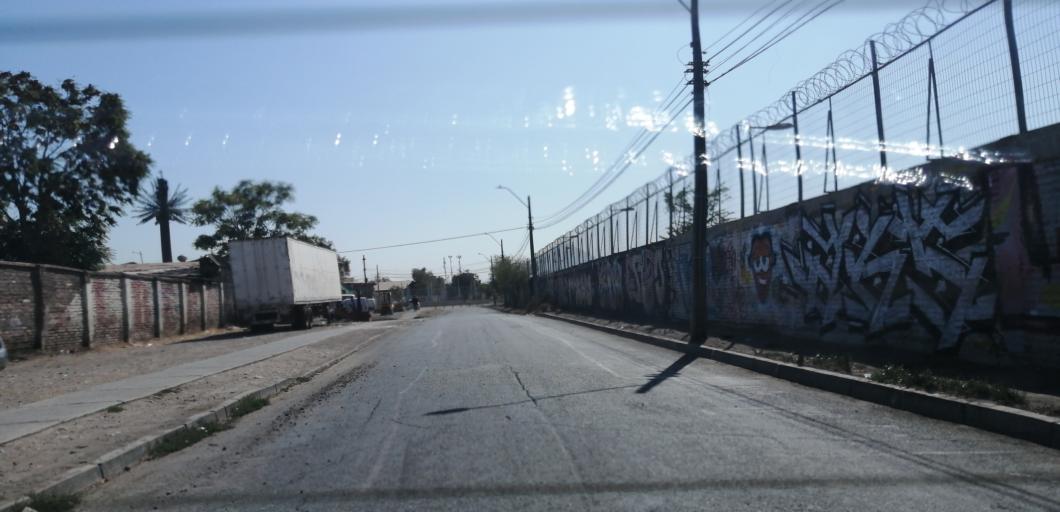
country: CL
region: Santiago Metropolitan
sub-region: Provincia de Santiago
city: Lo Prado
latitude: -33.4433
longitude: -70.7492
